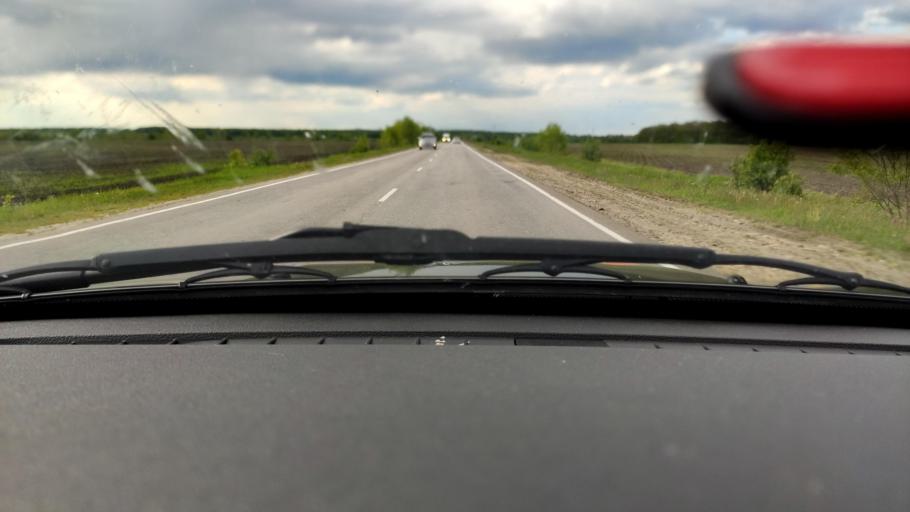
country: RU
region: Voronezj
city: Shilovo
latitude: 51.4440
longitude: 38.9945
